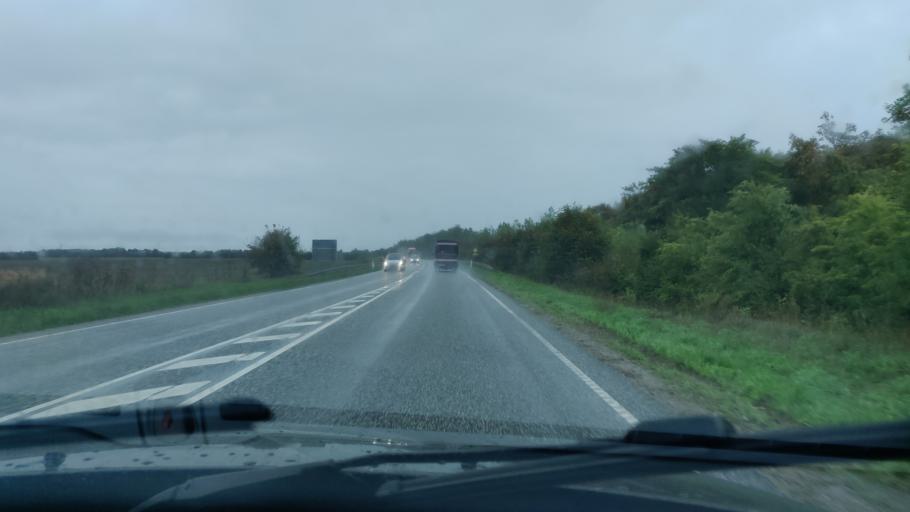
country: DK
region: North Denmark
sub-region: Thisted Kommune
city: Thisted
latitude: 56.9706
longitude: 8.7171
